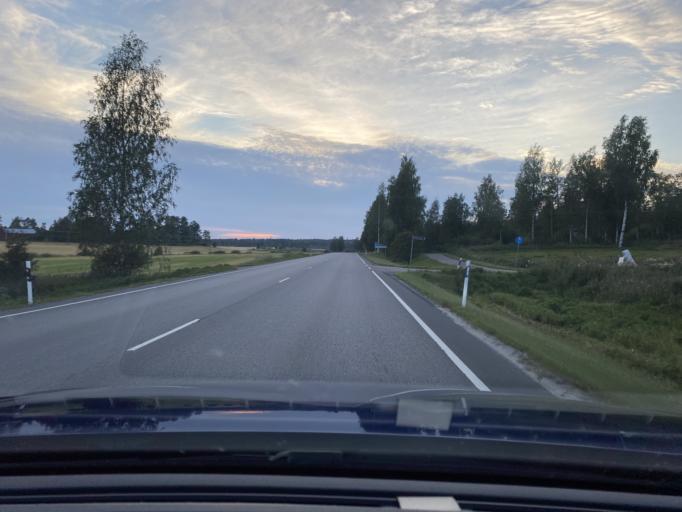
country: FI
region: Satakunta
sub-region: Pohjois-Satakunta
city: Kankaanpaeae
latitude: 61.7841
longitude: 22.4284
